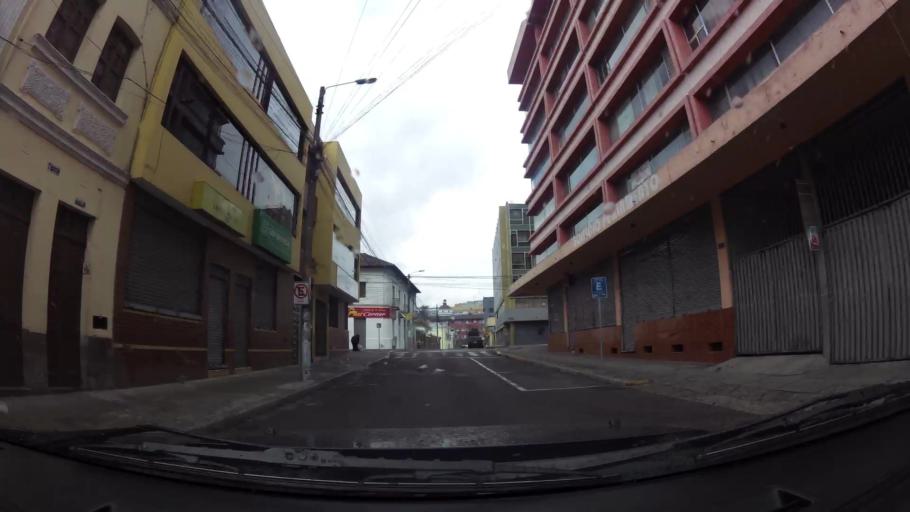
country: EC
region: Pichincha
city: Quito
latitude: -0.2131
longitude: -78.5007
